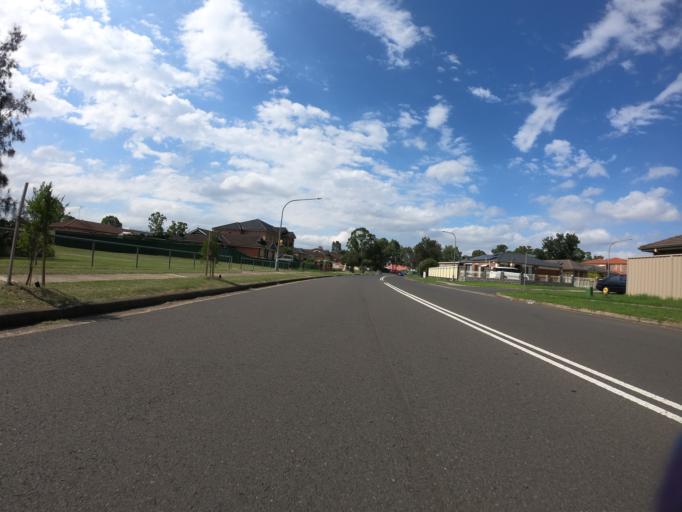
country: AU
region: New South Wales
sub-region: Blacktown
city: Hassall Grove
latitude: -33.7370
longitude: 150.8364
